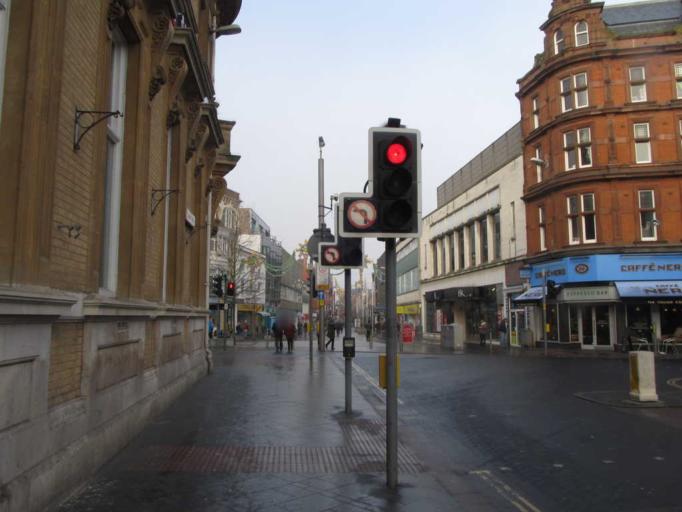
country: GB
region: England
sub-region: City of Leicester
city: Leicester
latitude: 52.6343
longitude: -1.1313
